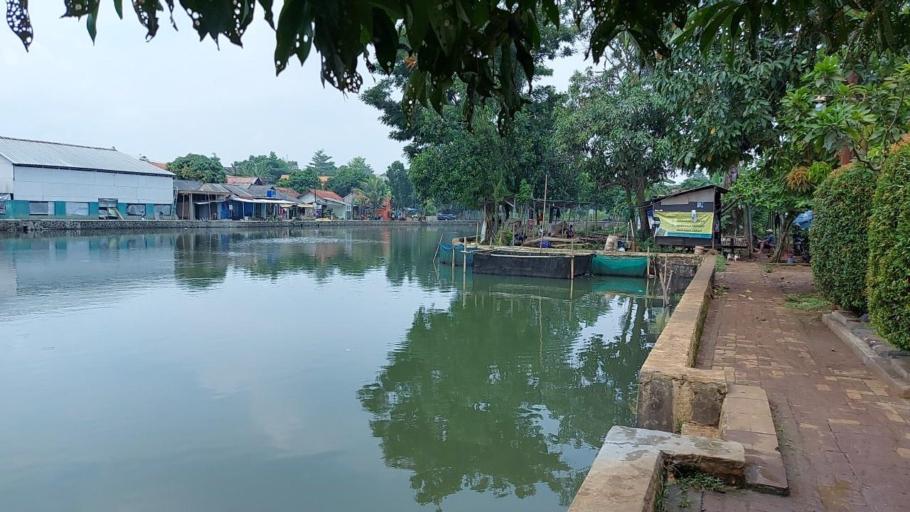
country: ID
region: West Java
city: Cibinong
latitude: -6.5290
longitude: 106.8159
